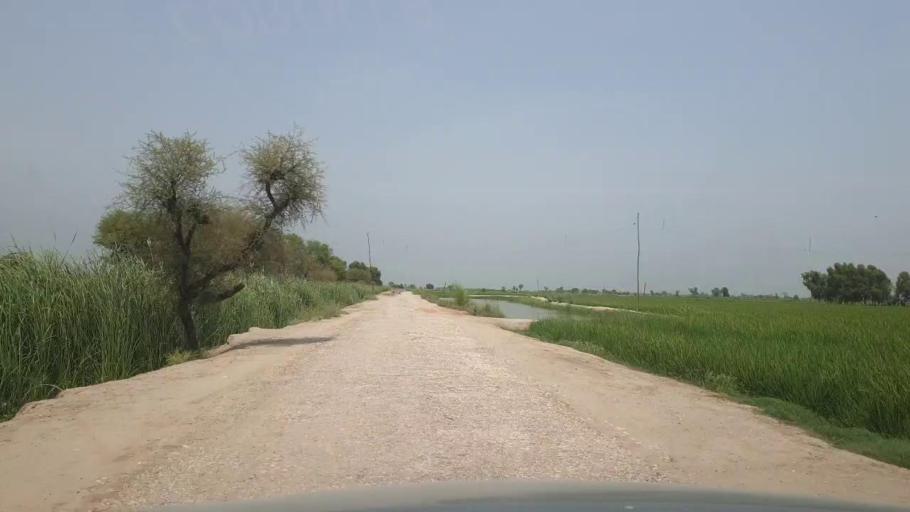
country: PK
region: Sindh
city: Garhi Yasin
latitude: 27.9246
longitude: 68.4336
